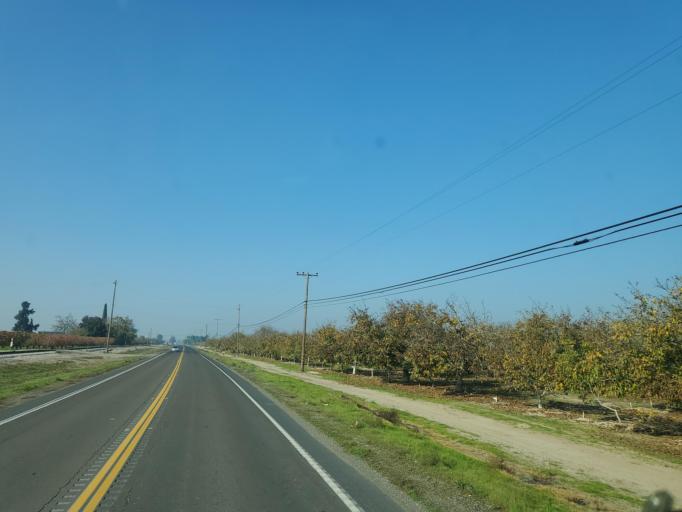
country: US
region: California
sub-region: San Joaquin County
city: Manteca
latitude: 37.8339
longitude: -121.1547
